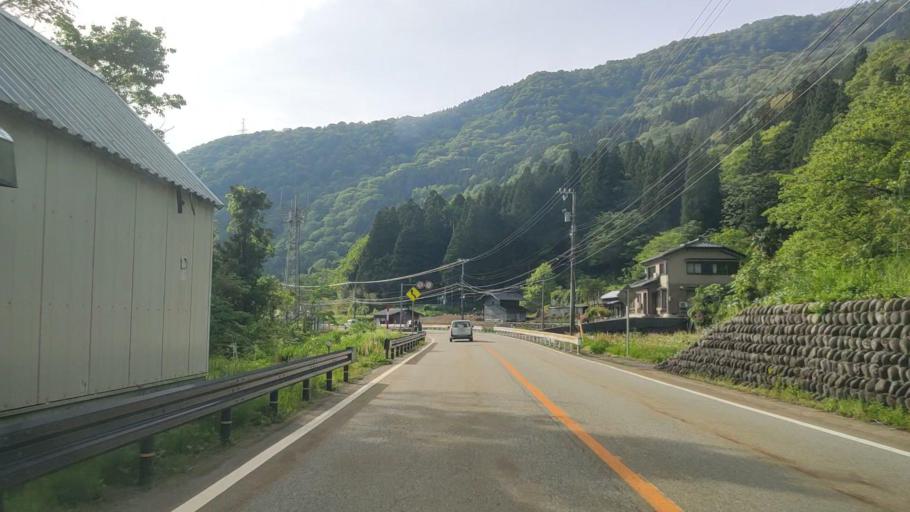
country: JP
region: Toyama
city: Yatsuomachi-higashikumisaka
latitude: 36.4487
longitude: 137.2719
